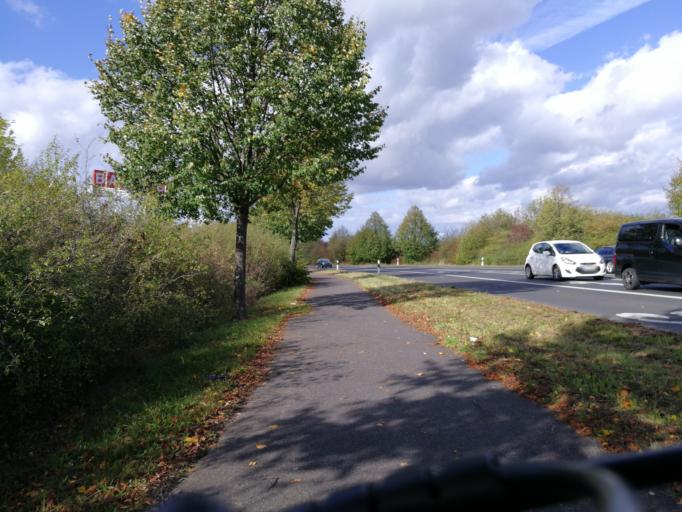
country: DE
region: North Rhine-Westphalia
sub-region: Regierungsbezirk Dusseldorf
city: Dusseldorf
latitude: 51.1452
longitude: 6.7578
